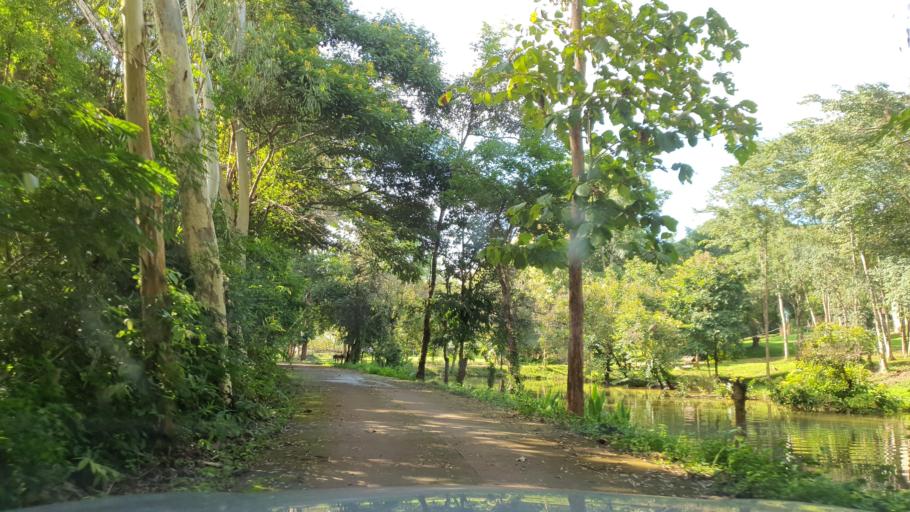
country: TH
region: Chiang Mai
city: Mae On
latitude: 18.7343
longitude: 99.3080
